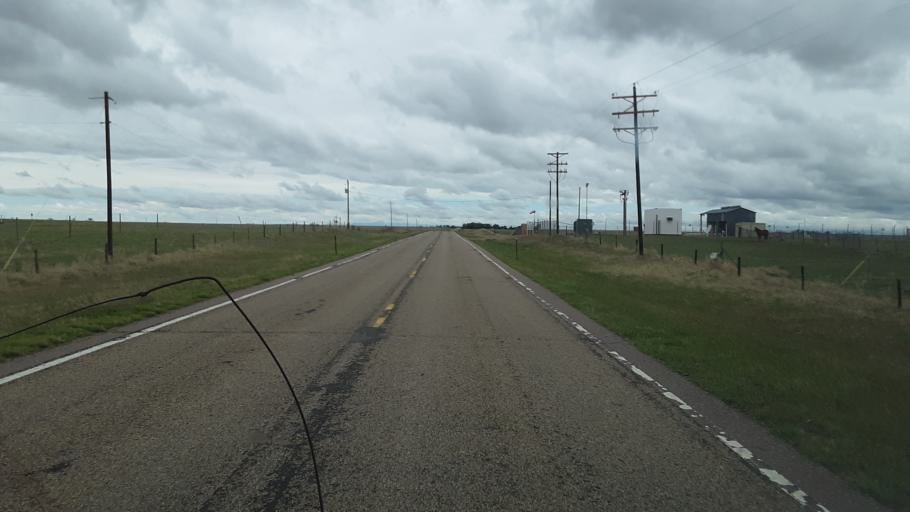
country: US
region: Colorado
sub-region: El Paso County
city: Ellicott
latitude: 38.8398
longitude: -104.0307
